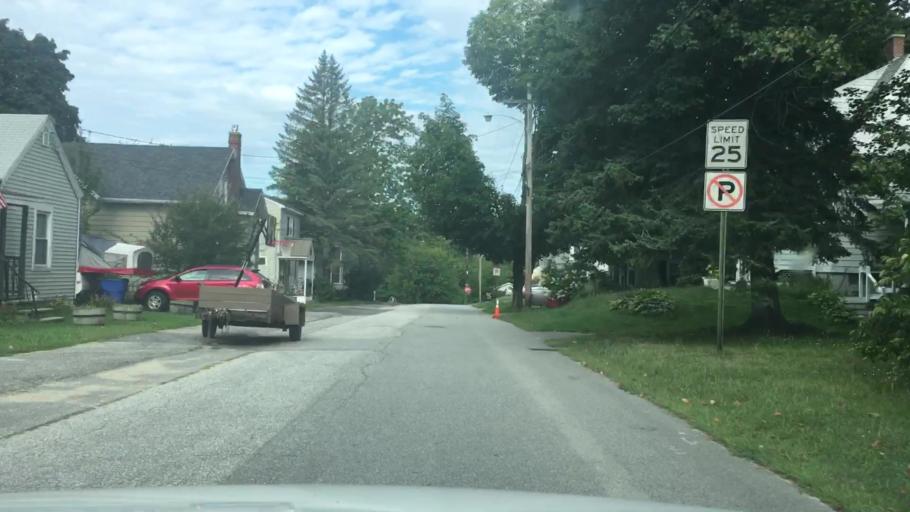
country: US
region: Maine
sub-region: Androscoggin County
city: Lewiston
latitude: 44.1039
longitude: -70.1895
